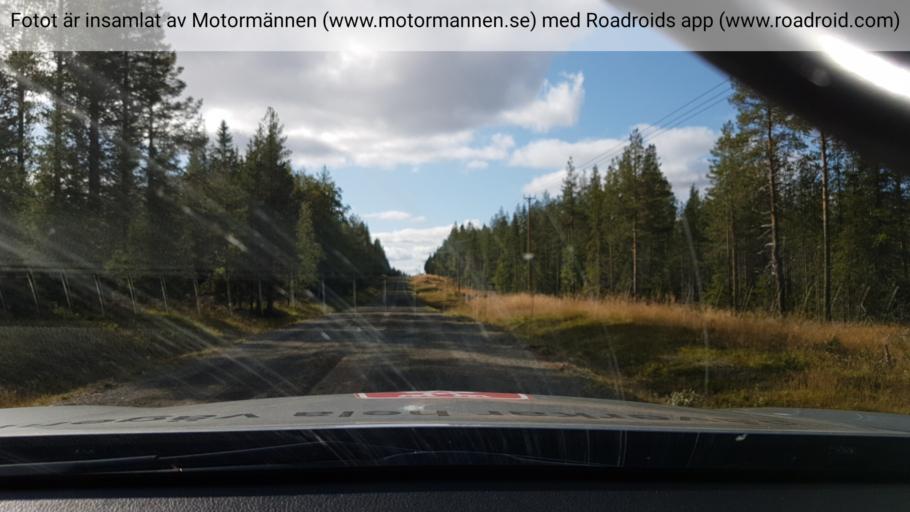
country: SE
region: Vaesterbotten
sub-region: Mala Kommun
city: Mala
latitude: 65.4898
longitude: 18.2487
